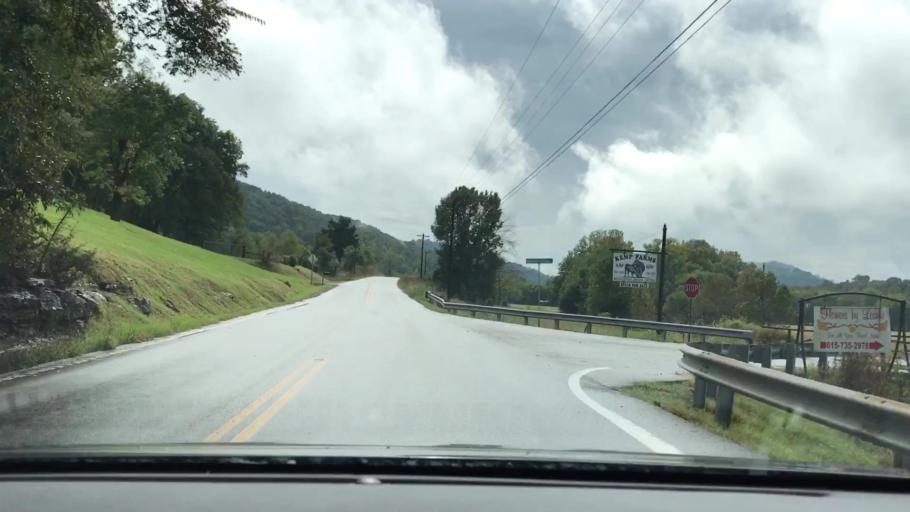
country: US
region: Tennessee
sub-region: Smith County
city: Carthage
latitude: 36.3236
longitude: -85.9676
